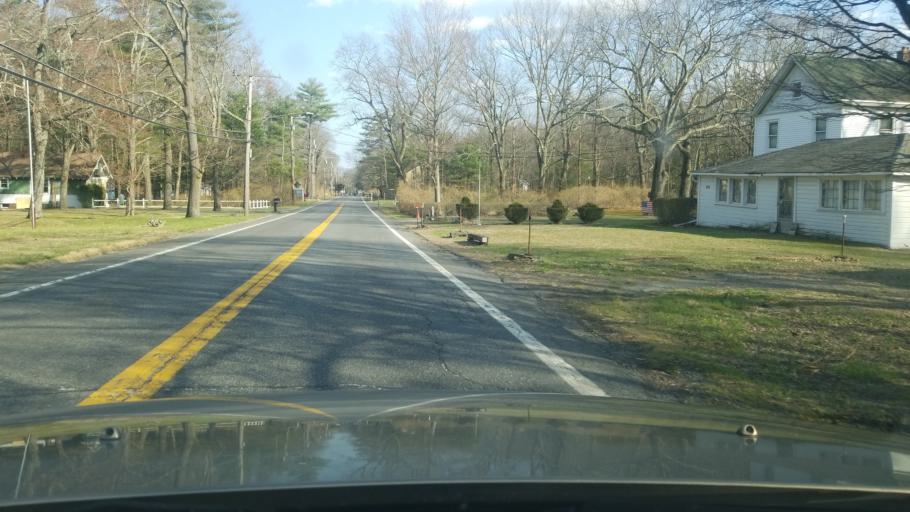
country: US
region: New York
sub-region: Greene County
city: Palenville
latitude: 42.1657
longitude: -74.0143
